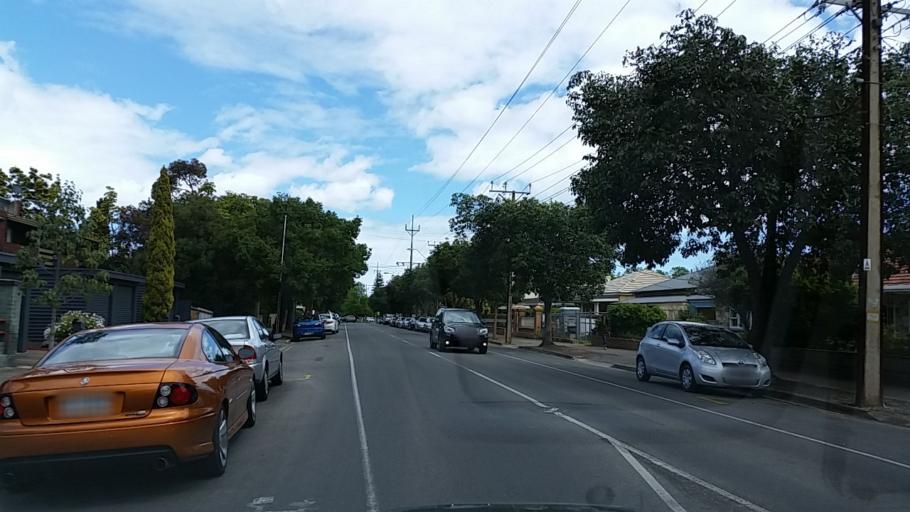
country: AU
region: South Australia
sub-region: Norwood Payneham St Peters
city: Trinity Gardens
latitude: -34.9182
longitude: 138.6340
